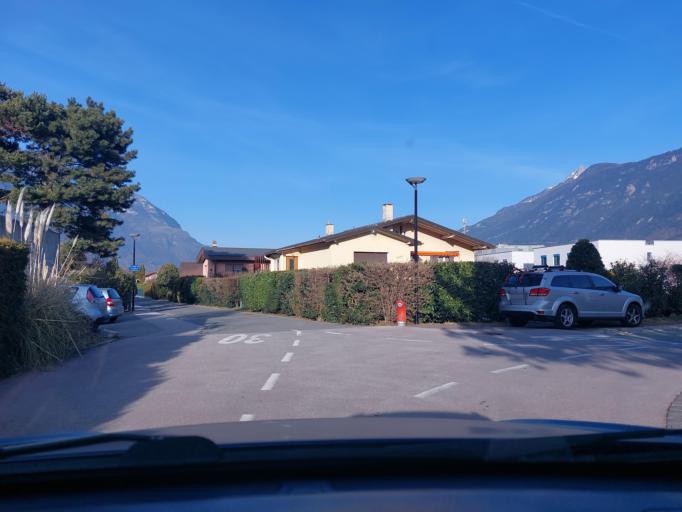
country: CH
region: Valais
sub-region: Martigny District
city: Martigny-Ville
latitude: 46.1087
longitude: 7.0816
